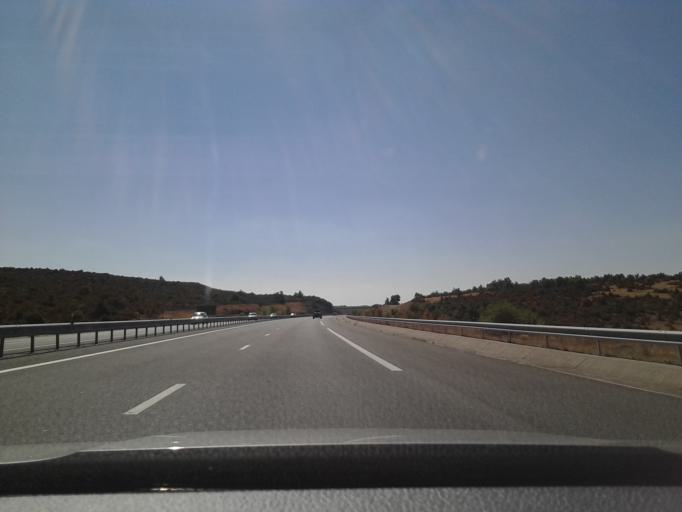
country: FR
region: Midi-Pyrenees
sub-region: Departement de l'Aveyron
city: Creissels
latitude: 44.0559
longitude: 3.0394
